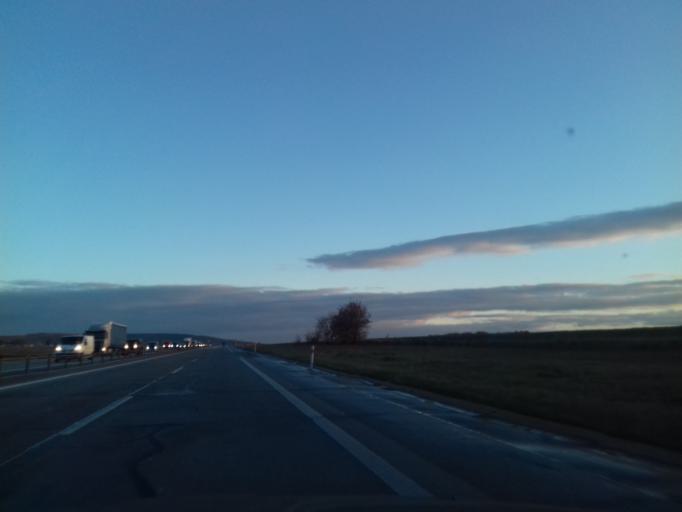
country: CZ
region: South Moravian
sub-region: Okres Vyskov
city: Vyskov
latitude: 49.2913
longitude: 17.0221
